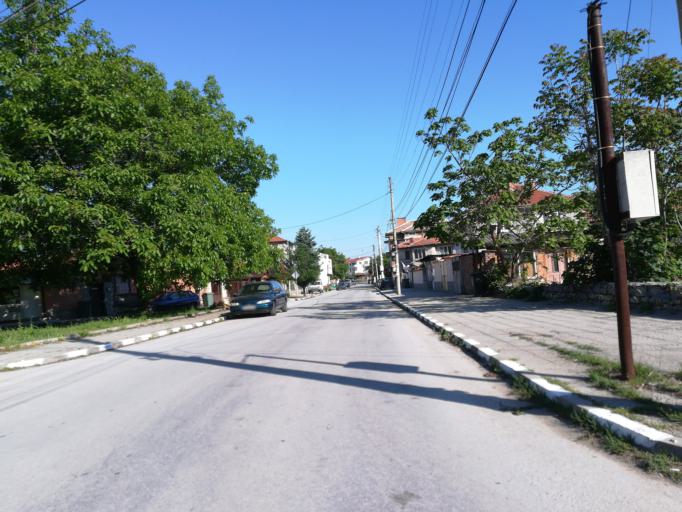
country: BG
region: Stara Zagora
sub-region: Obshtina Chirpan
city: Chirpan
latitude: 42.1030
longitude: 25.2222
